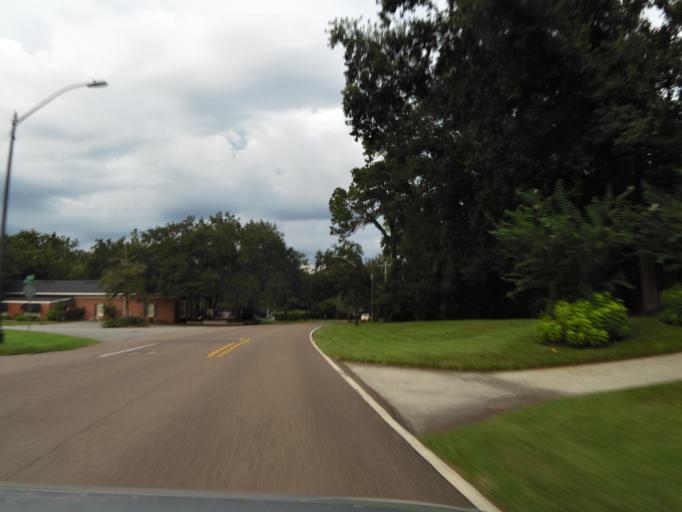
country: US
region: Florida
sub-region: Duval County
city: Jacksonville
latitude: 30.2701
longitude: -81.7032
